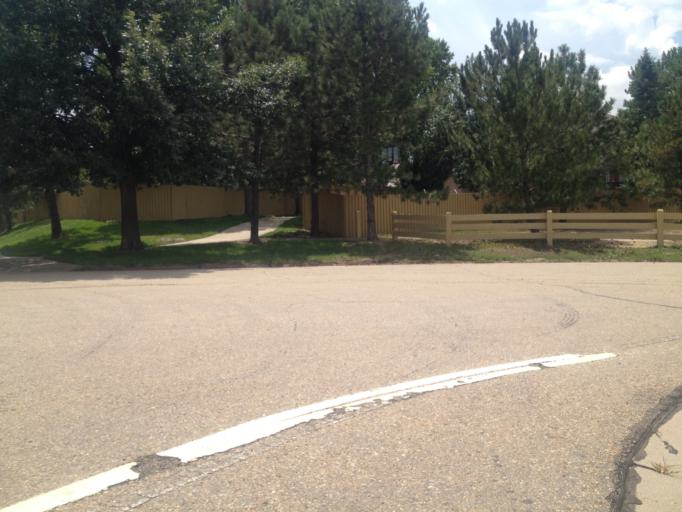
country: US
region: Colorado
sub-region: Boulder County
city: Superior
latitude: 39.9436
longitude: -105.1471
